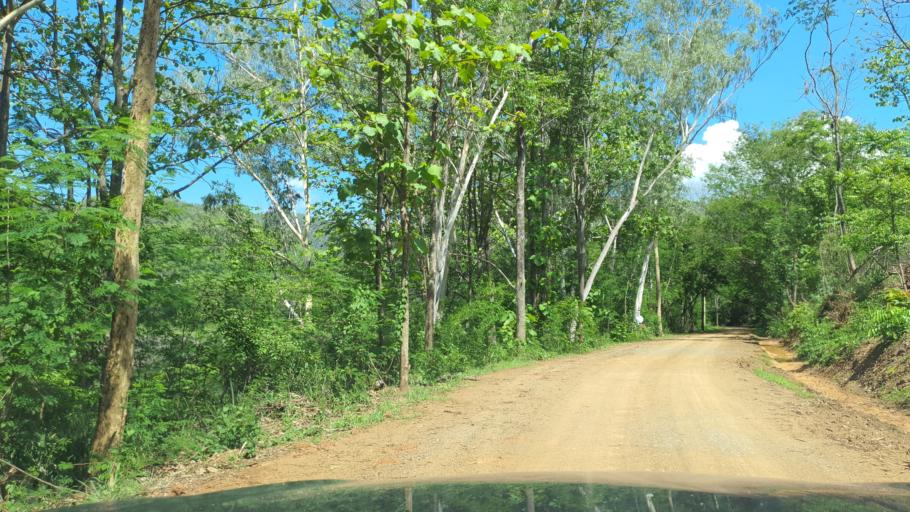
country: TH
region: Chiang Mai
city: Mae On
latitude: 18.8048
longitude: 99.2655
